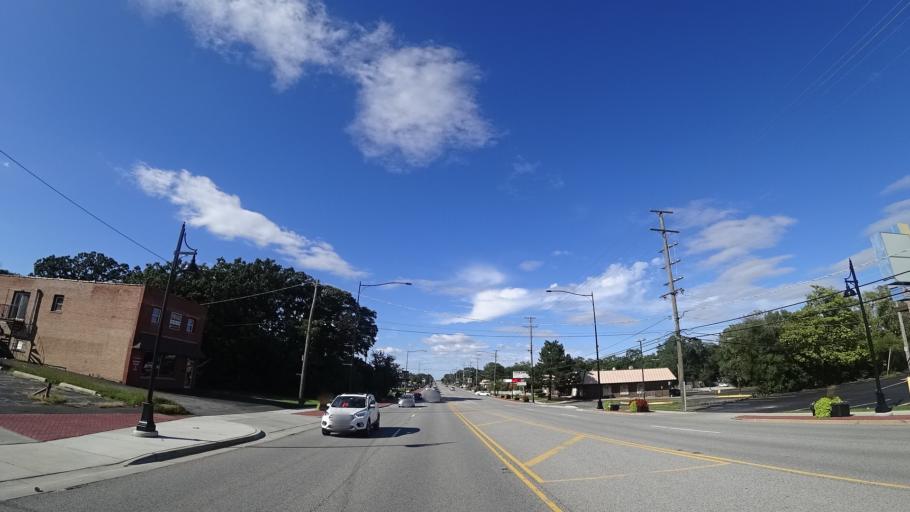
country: US
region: Illinois
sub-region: Cook County
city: Oak Forest
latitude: 41.6133
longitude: -87.7369
